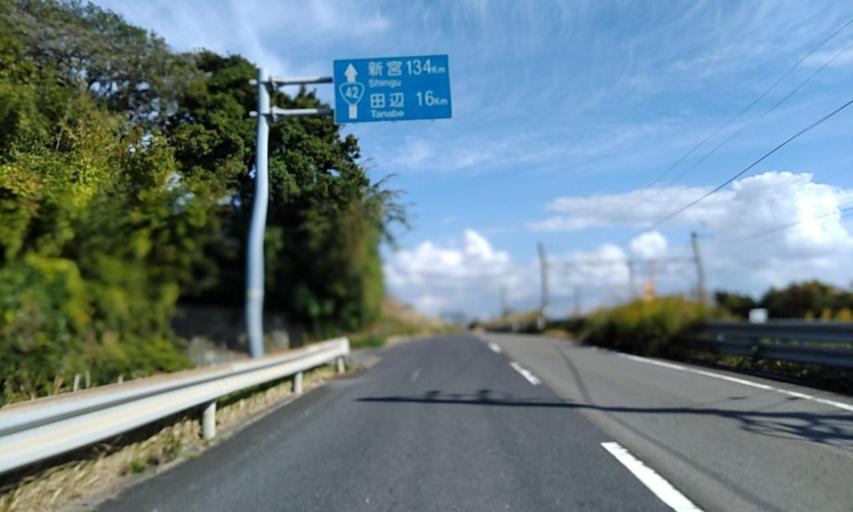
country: JP
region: Wakayama
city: Tanabe
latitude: 33.7834
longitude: 135.2570
